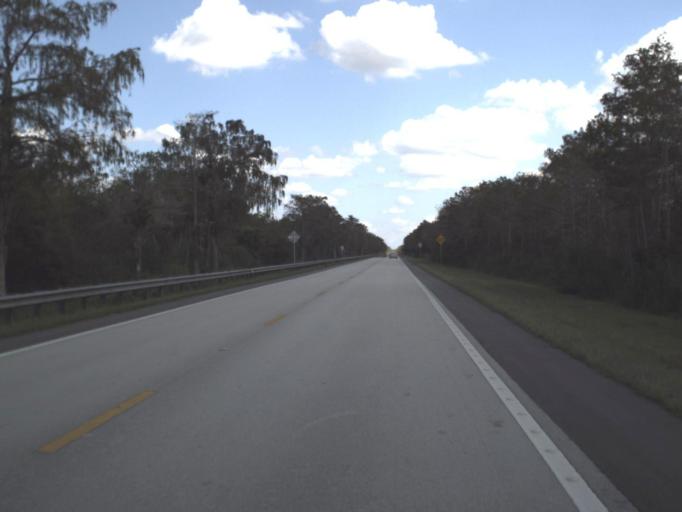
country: US
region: Florida
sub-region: Miami-Dade County
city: Kendall West
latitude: 25.8482
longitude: -80.9478
